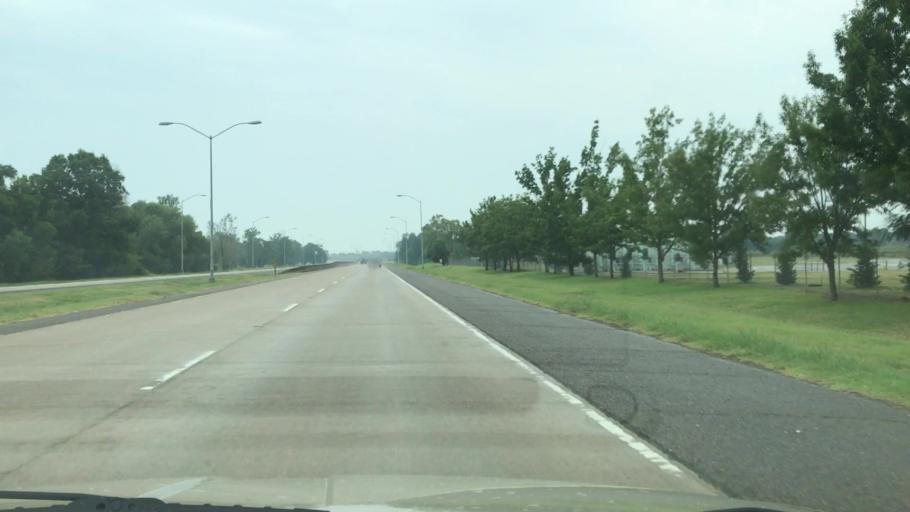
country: US
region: Louisiana
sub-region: Bossier Parish
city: Bossier City
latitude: 32.4818
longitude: -93.6835
